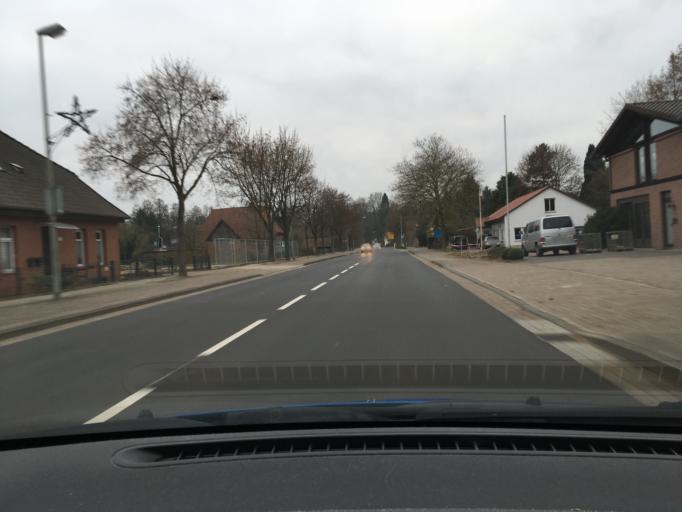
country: DE
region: Lower Saxony
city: Bad Fallingbostel
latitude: 52.9067
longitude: 9.7655
